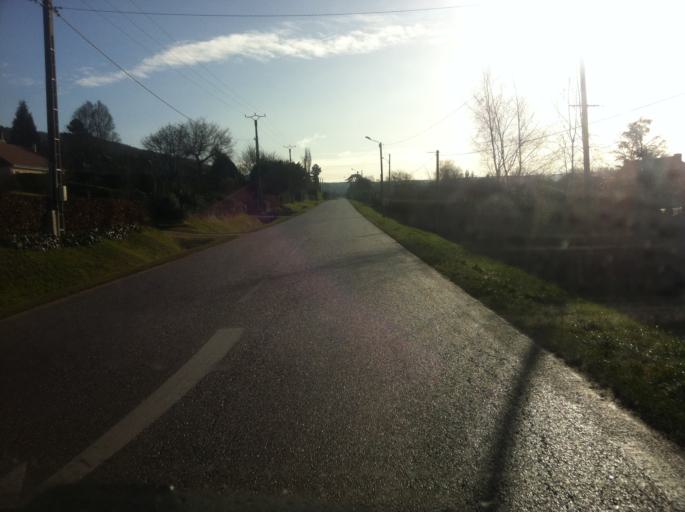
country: FR
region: Haute-Normandie
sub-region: Departement de la Seine-Maritime
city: Henouville
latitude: 49.4739
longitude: 0.9461
